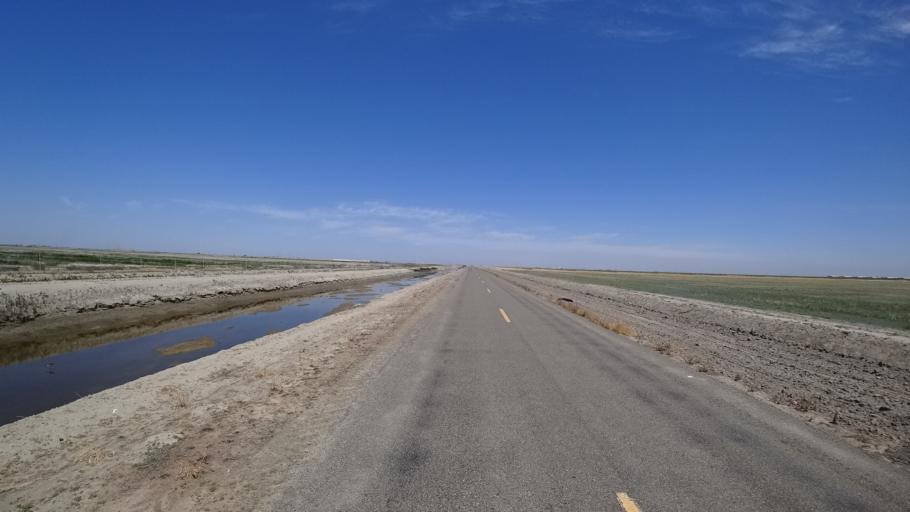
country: US
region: California
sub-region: Kings County
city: Corcoran
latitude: 36.1284
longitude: -119.6802
